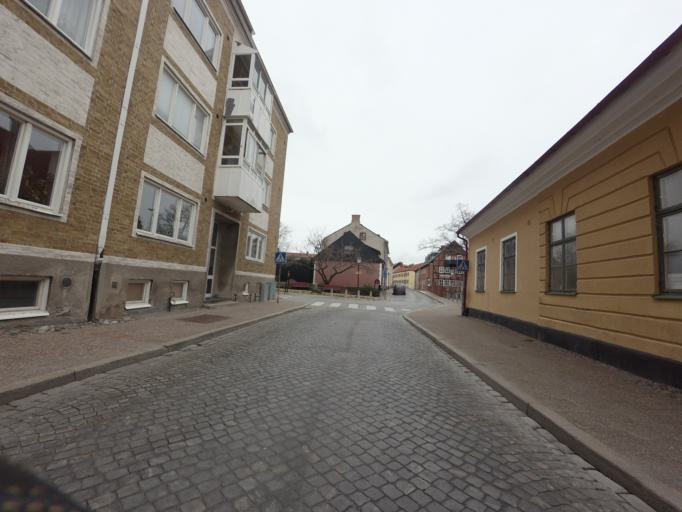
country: SE
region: Skane
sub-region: Ystads Kommun
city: Ystad
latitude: 55.4308
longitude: 13.8190
